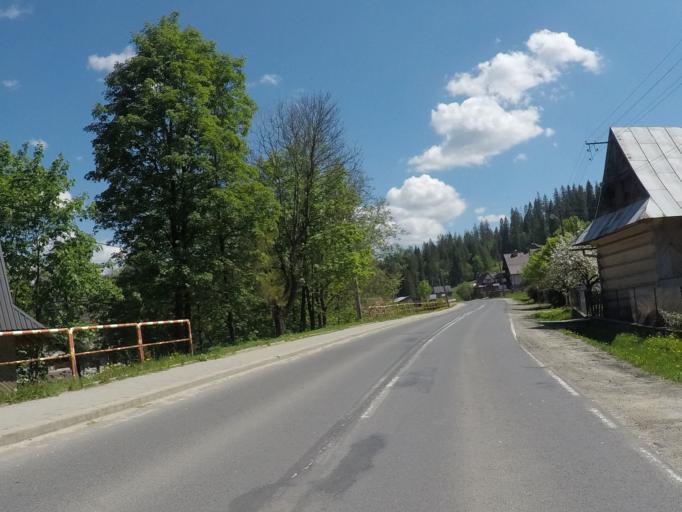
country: PL
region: Lesser Poland Voivodeship
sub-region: Powiat tatrzanski
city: Bukowina Tatrzanska
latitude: 49.3350
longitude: 20.0679
